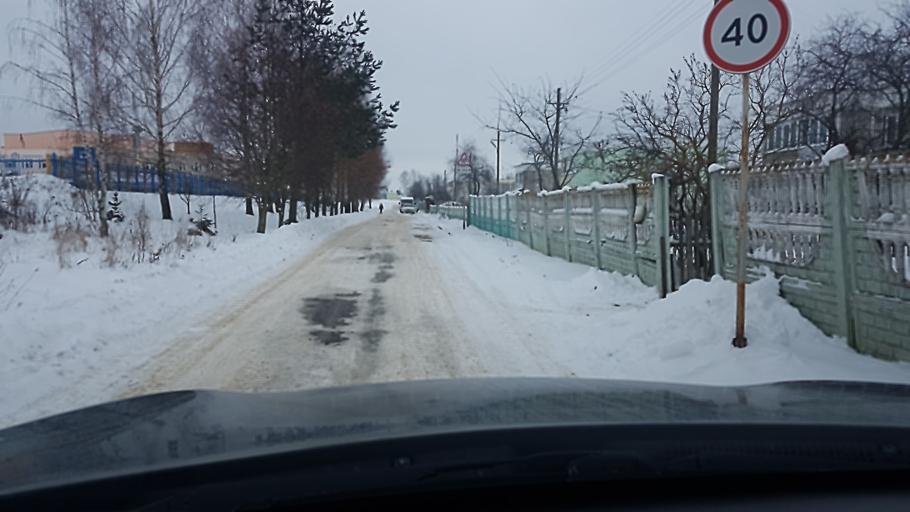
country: BY
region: Minsk
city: Azyartso
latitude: 53.8444
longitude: 27.3913
